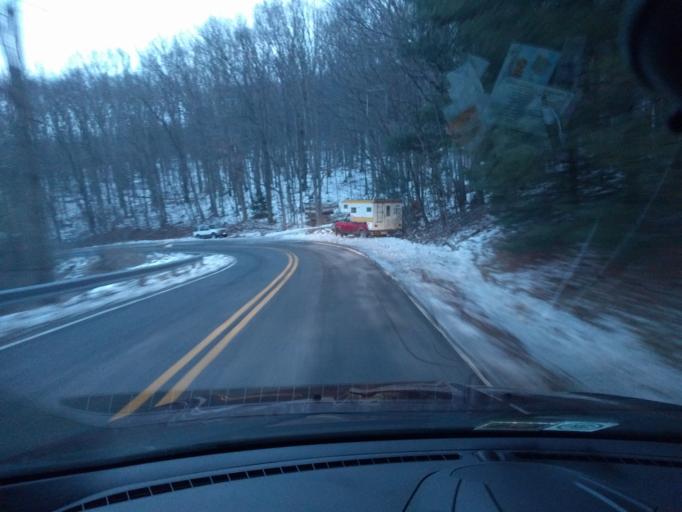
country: US
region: Virginia
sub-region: Alleghany County
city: Clifton Forge
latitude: 37.8961
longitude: -79.8891
